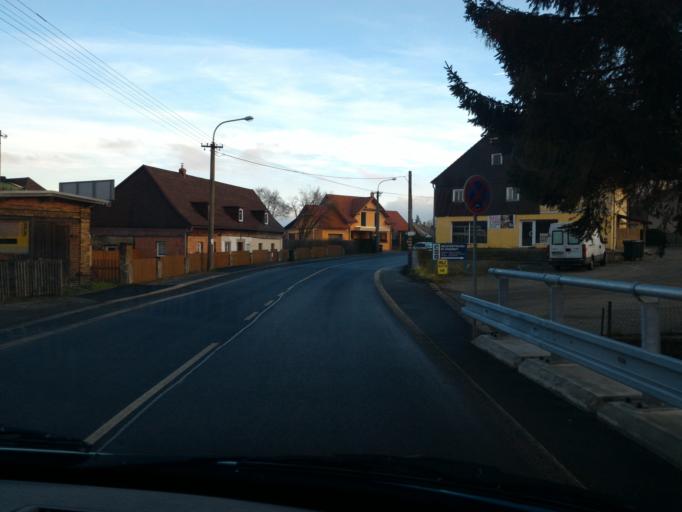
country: CZ
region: Ustecky
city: Varnsdorf
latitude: 50.9167
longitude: 14.6074
